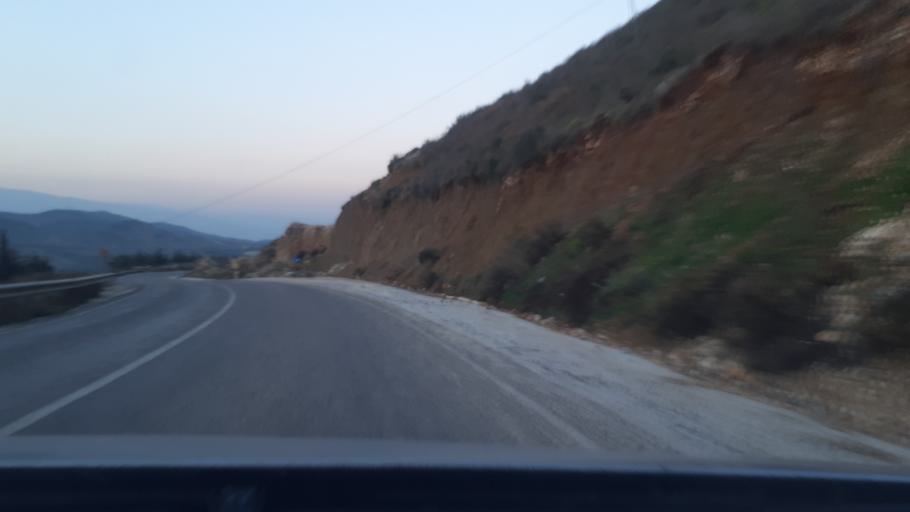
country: TR
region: Hatay
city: Dursunlu
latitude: 36.1713
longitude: 36.1865
